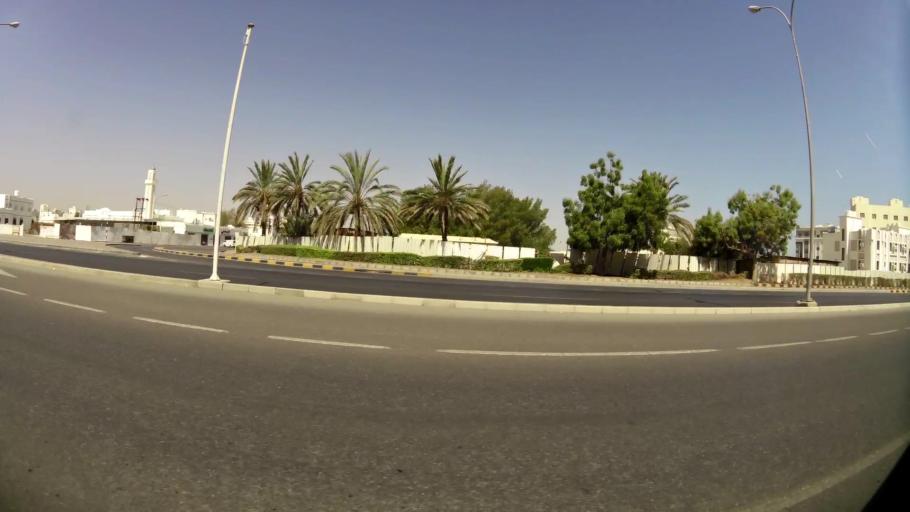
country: OM
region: Muhafazat Masqat
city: Bawshar
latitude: 23.5814
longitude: 58.4073
